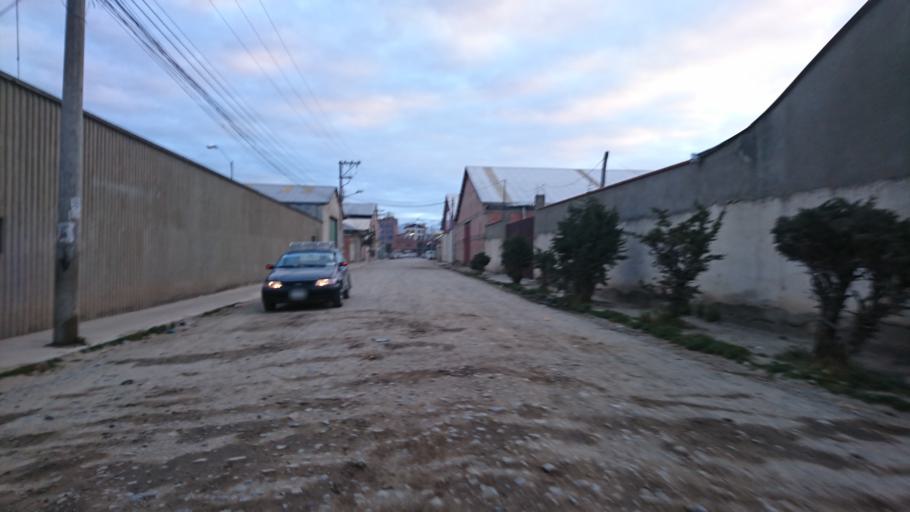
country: BO
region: La Paz
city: La Paz
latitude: -16.4992
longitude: -68.1848
